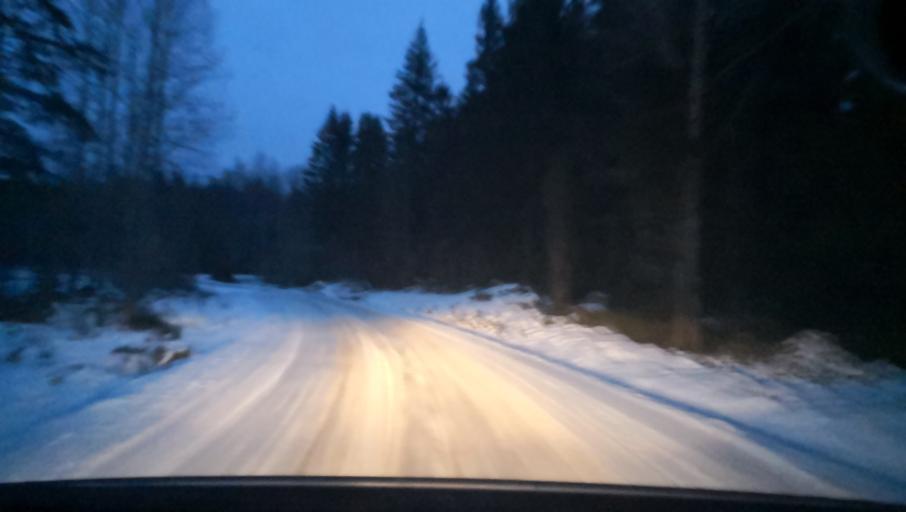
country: SE
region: Uppsala
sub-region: Heby Kommun
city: Tarnsjo
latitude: 60.2412
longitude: 16.6991
